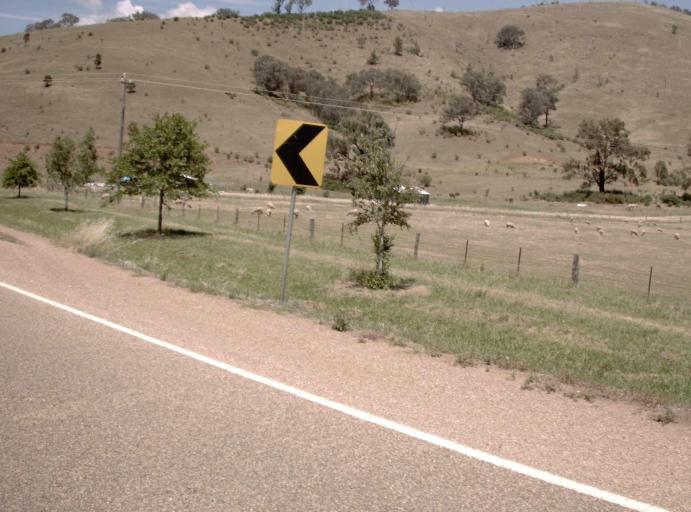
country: AU
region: Victoria
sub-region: East Gippsland
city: Bairnsdale
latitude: -37.2563
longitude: 147.7112
